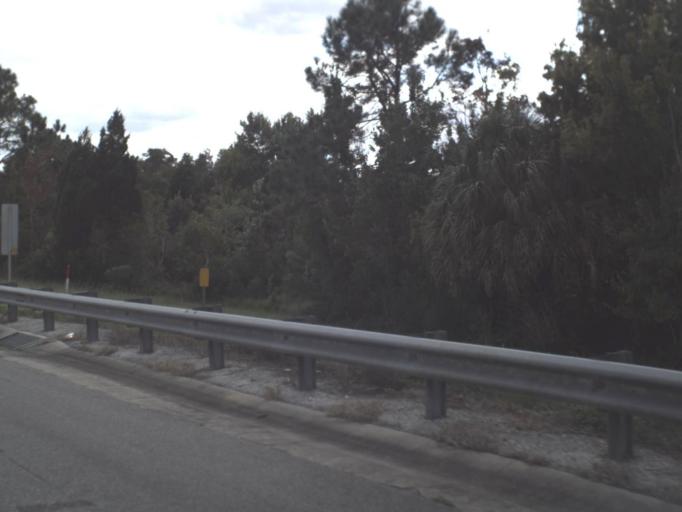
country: US
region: Florida
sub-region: Osceola County
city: Saint Cloud
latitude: 28.1483
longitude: -81.2962
